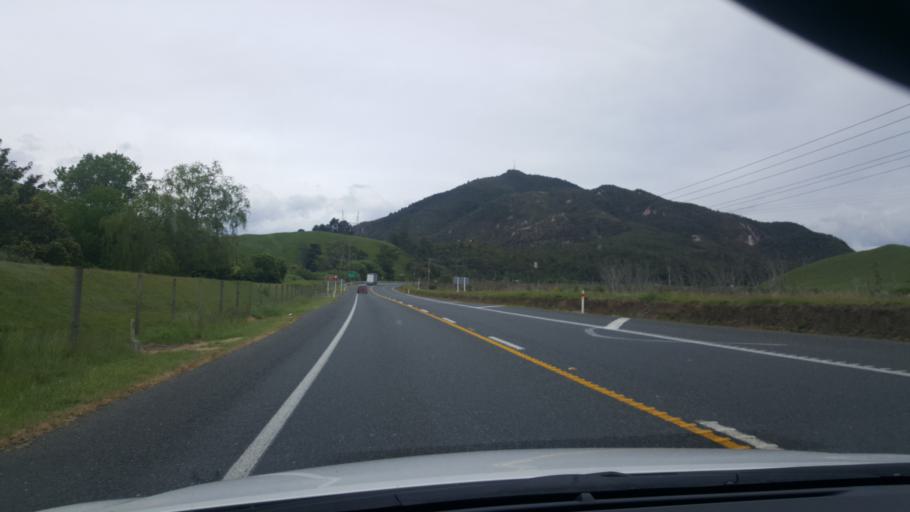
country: NZ
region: Bay of Plenty
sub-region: Rotorua District
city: Rotorua
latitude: -38.3066
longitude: 176.3721
